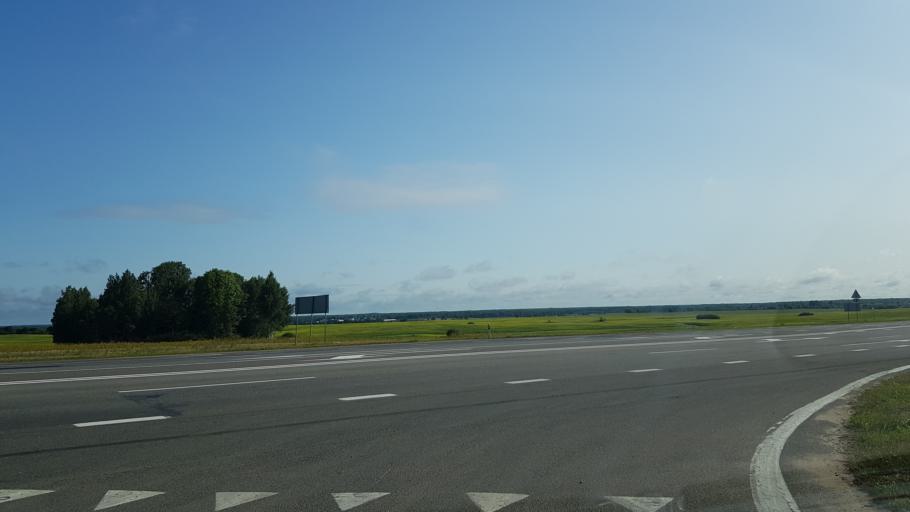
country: BY
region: Vitebsk
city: Dubrowna
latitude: 54.6351
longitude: 30.5331
